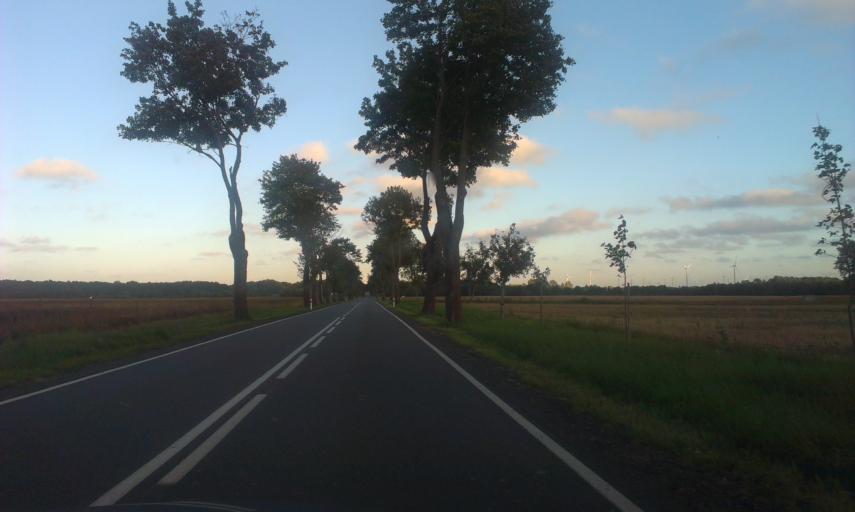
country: PL
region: West Pomeranian Voivodeship
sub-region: Powiat slawienski
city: Darlowo
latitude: 54.3558
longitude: 16.5198
